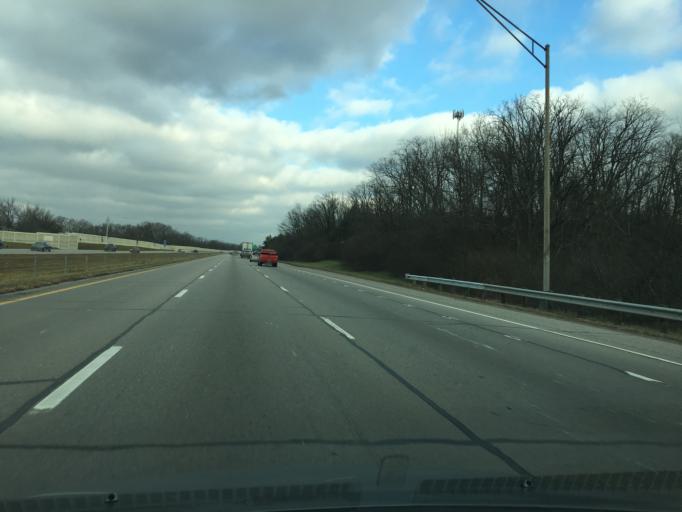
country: US
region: Ohio
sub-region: Hamilton County
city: Pleasant Run
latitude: 39.2881
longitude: -84.5592
